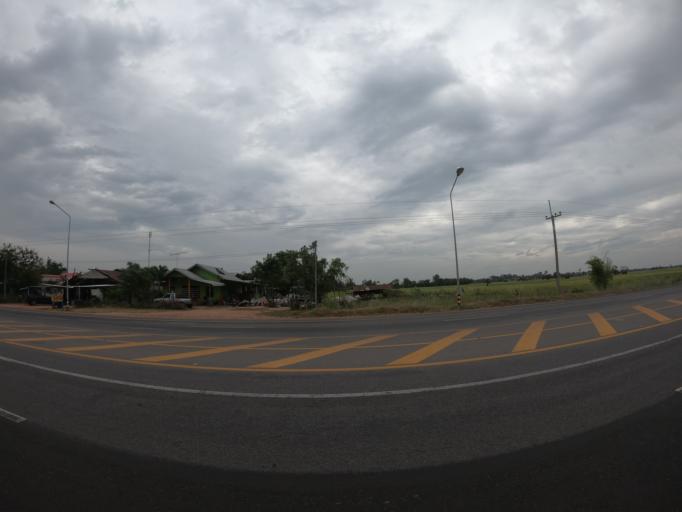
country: TH
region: Roi Et
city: Chiang Khwan
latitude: 16.1005
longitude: 103.8021
